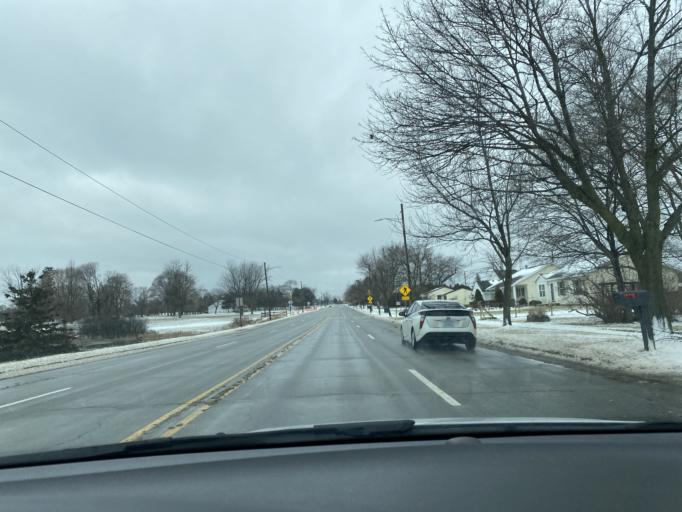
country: US
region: Michigan
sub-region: Lapeer County
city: Lapeer
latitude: 43.0504
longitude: -83.3365
